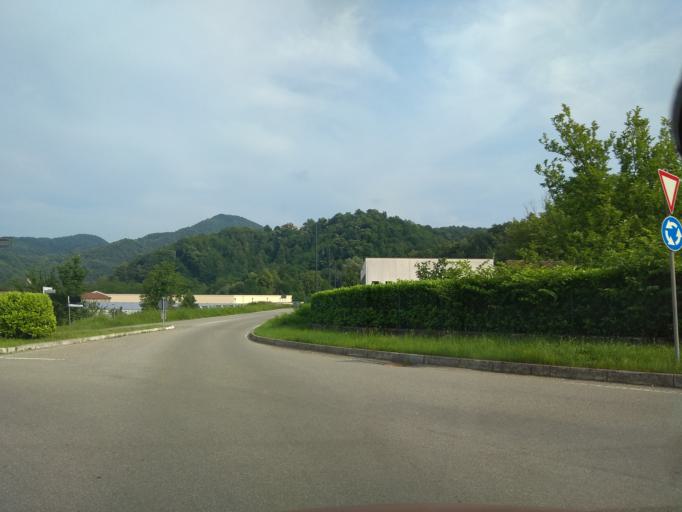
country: IT
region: Piedmont
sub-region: Provincia di Biella
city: Pray
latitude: 45.6751
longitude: 8.1990
